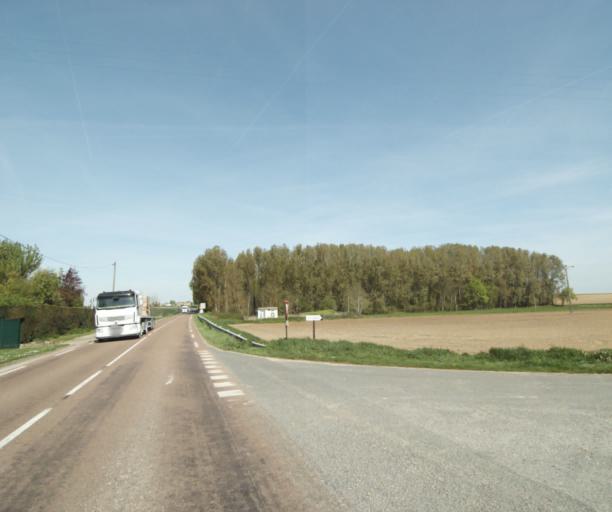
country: FR
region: Ile-de-France
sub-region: Departement de Seine-et-Marne
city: Nangis
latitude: 48.5425
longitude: 3.0177
